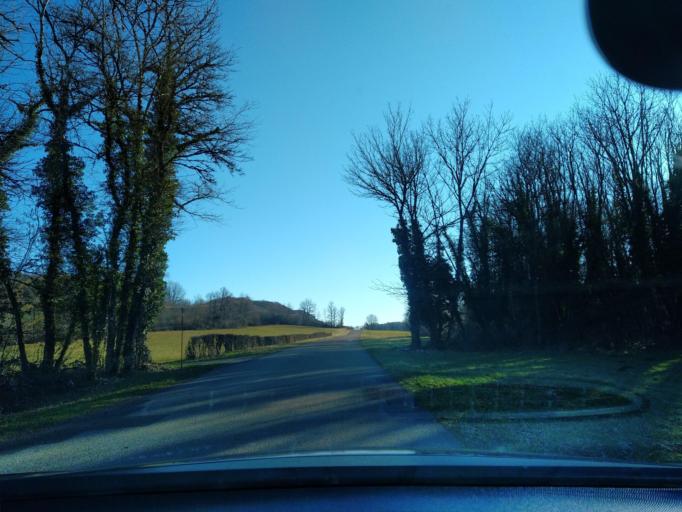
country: FR
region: Franche-Comte
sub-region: Departement du Jura
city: Poligny
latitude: 46.7143
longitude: 5.7383
